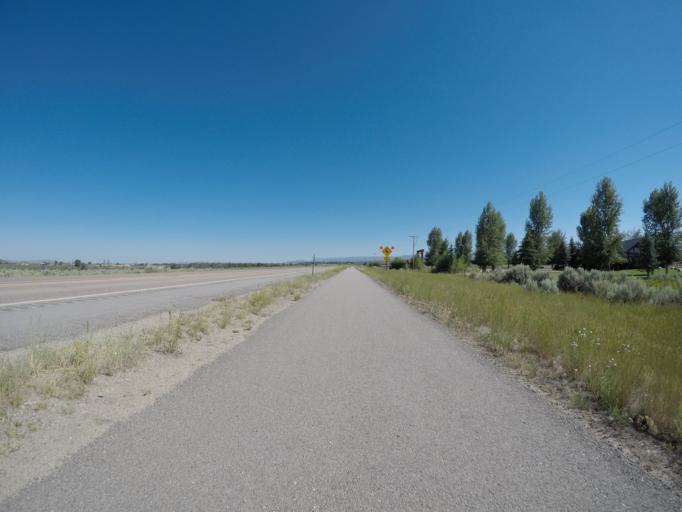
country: US
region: Wyoming
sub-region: Sublette County
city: Pinedale
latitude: 42.8392
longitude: -109.8465
